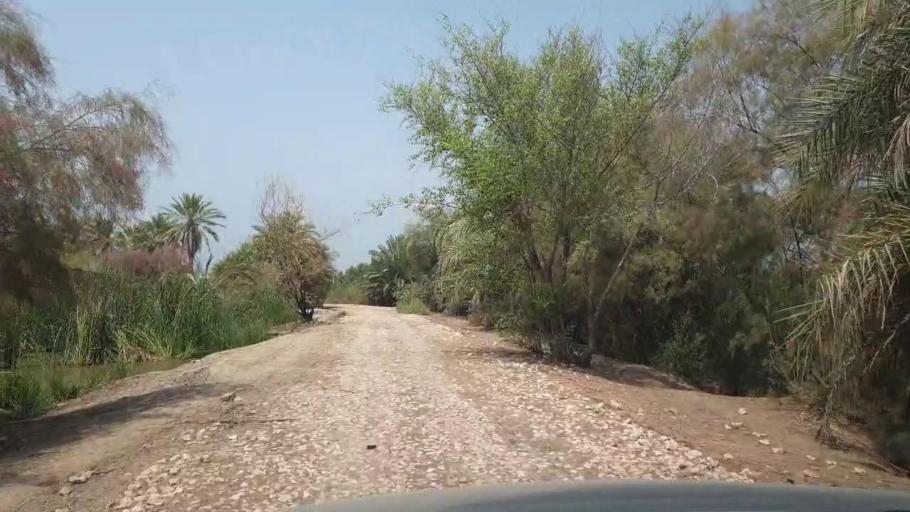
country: PK
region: Sindh
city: Madeji
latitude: 27.8140
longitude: 68.5232
